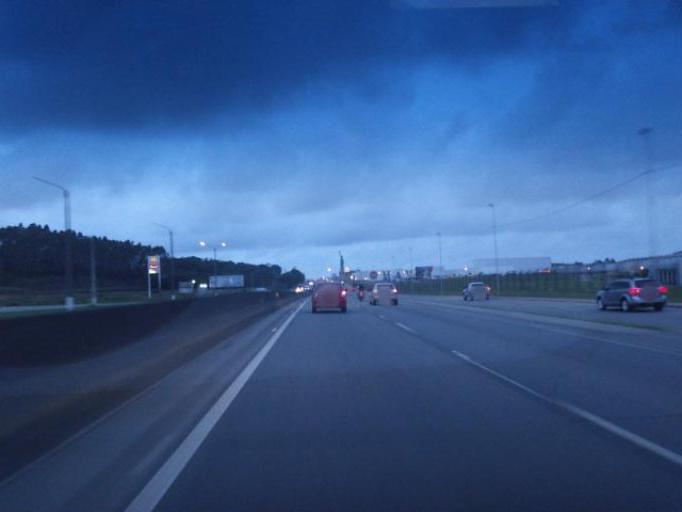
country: BR
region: Santa Catarina
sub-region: Barra Velha
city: Barra Velha
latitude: -26.6291
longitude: -48.7071
